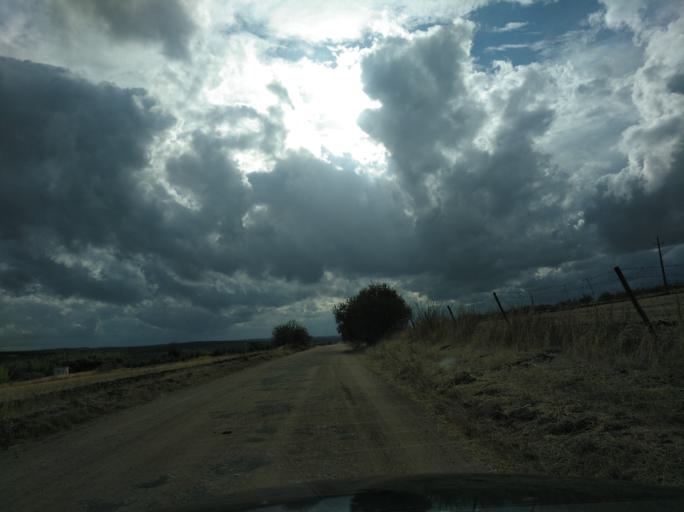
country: PT
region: Portalegre
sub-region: Campo Maior
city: Campo Maior
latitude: 39.0404
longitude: -7.1094
